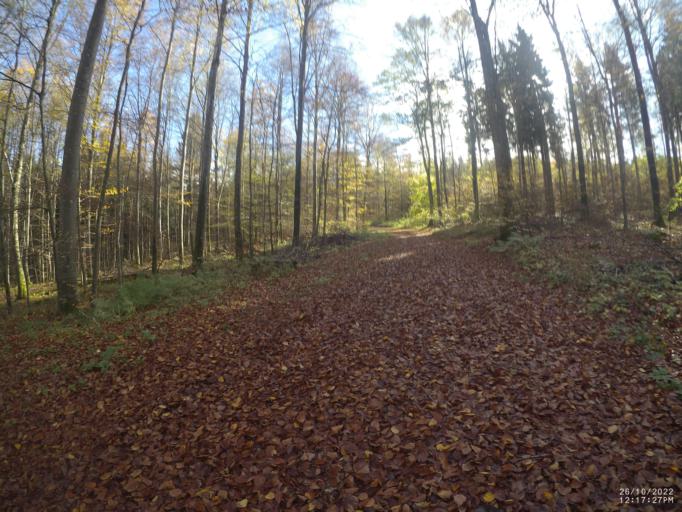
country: DE
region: Baden-Wuerttemberg
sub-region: Regierungsbezirk Stuttgart
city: Wiesensteig
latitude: 48.5442
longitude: 9.6051
